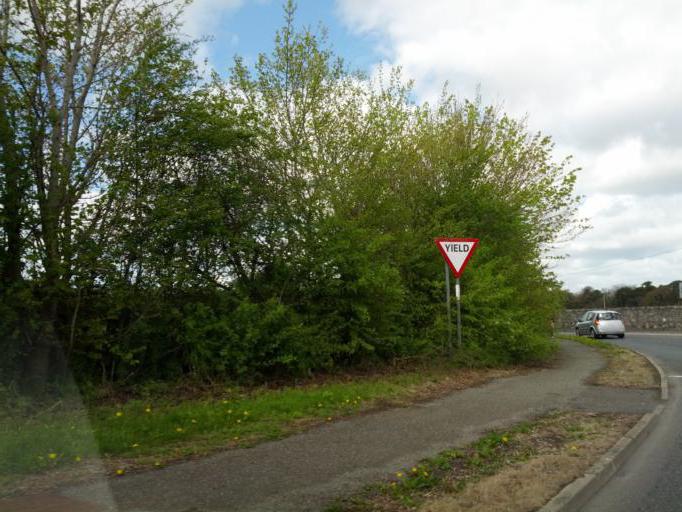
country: IE
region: Leinster
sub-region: Kildare
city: Leixlip
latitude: 53.3591
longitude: -6.4747
